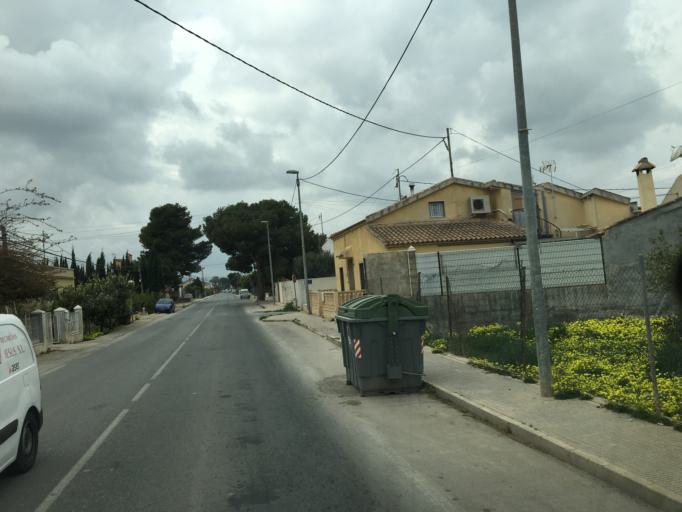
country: ES
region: Murcia
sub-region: Murcia
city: Beniel
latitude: 38.0279
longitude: -1.0269
